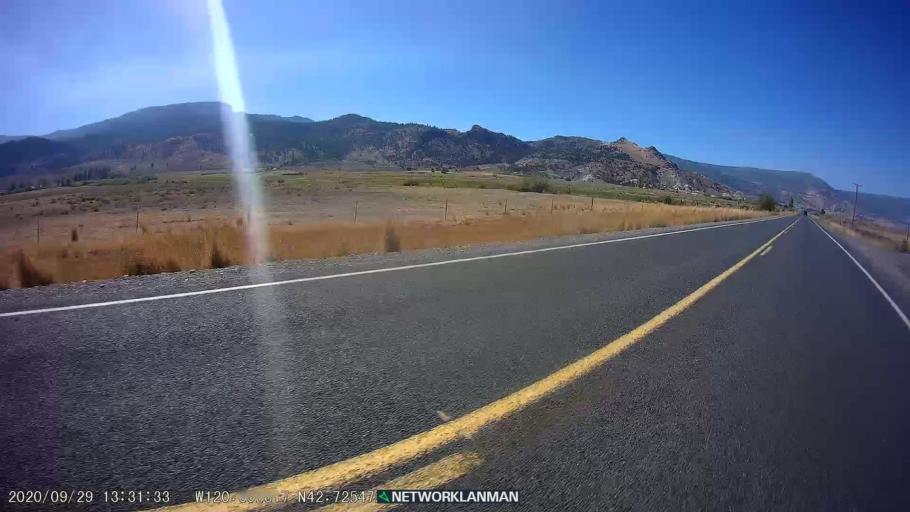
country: US
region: Oregon
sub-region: Lake County
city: Lakeview
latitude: 42.7256
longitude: -120.6963
